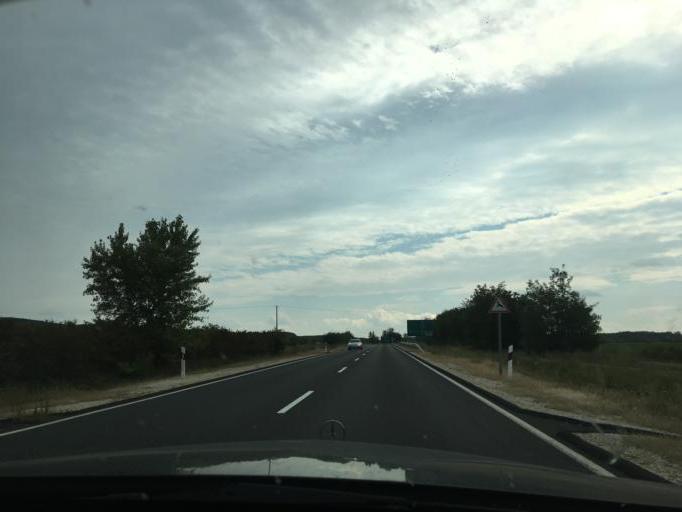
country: HU
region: Somogy
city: Balatonszarszo
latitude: 46.8245
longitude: 17.8535
